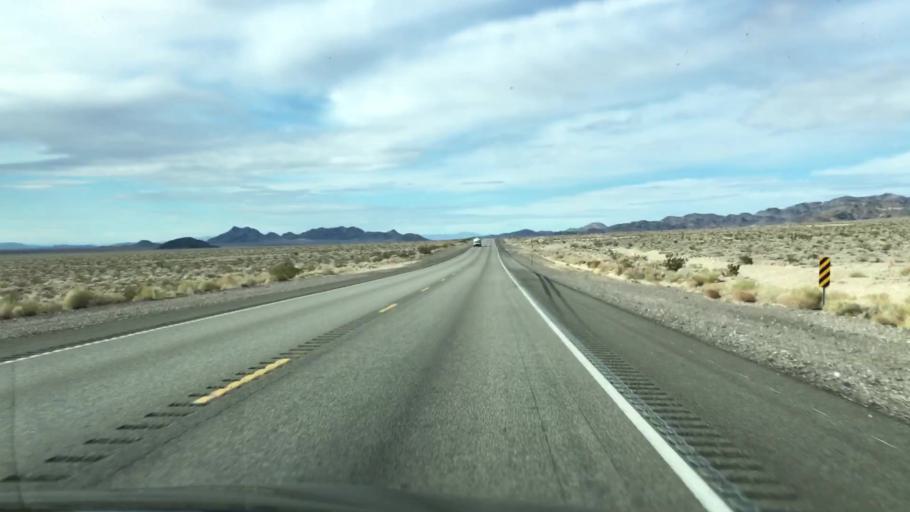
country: US
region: Nevada
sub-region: Nye County
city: Pahrump
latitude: 36.5842
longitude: -116.2098
